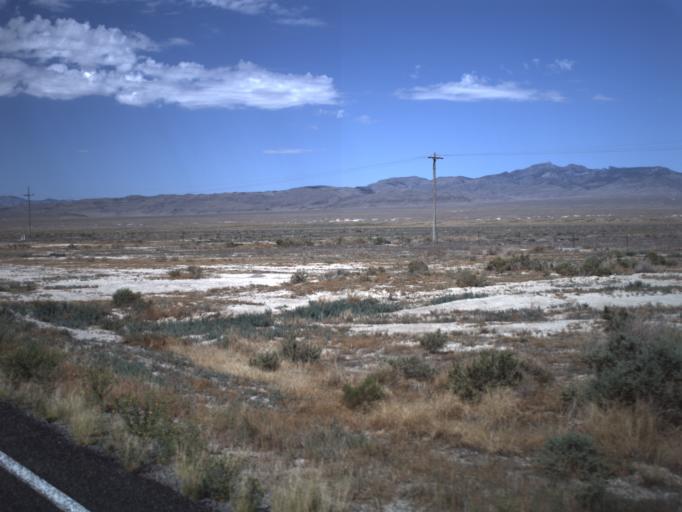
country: US
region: Utah
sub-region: Millard County
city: Delta
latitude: 39.0990
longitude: -113.1568
